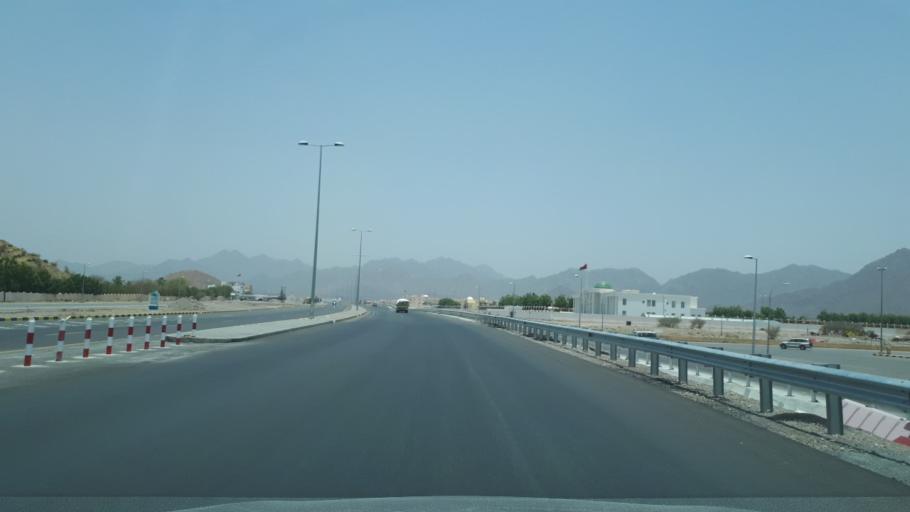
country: OM
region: Al Batinah
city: Rustaq
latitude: 23.4375
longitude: 57.4164
